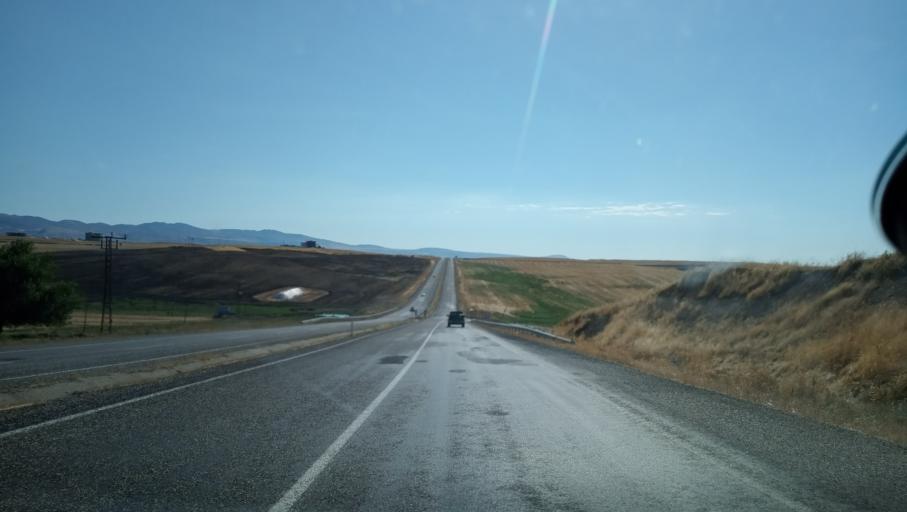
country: TR
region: Diyarbakir
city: Bagdere
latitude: 38.1281
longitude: 40.7822
